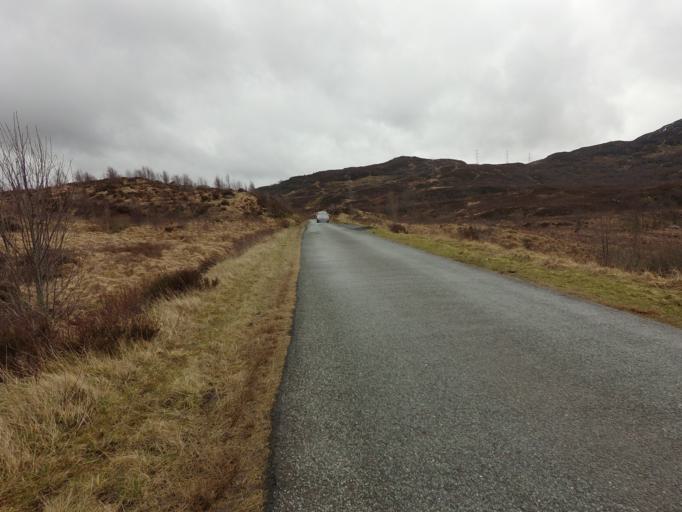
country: GB
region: Scotland
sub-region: West Dunbartonshire
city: Balloch
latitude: 56.2472
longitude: -4.5854
